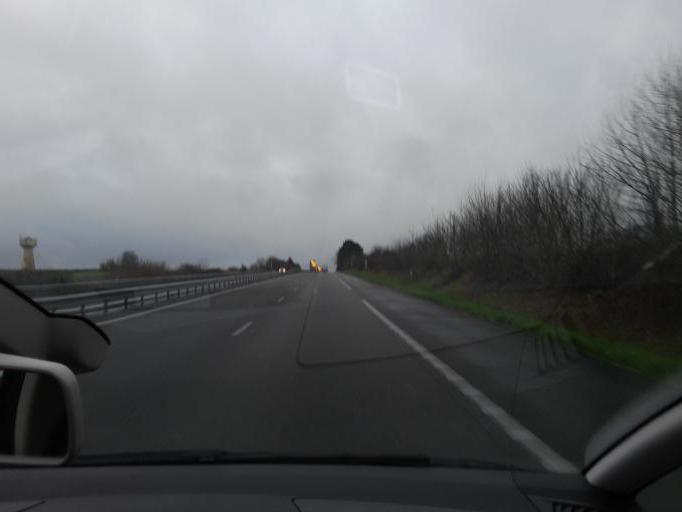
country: FR
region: Nord-Pas-de-Calais
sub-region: Departement du Pas-de-Calais
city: Hermies
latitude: 50.1142
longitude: 3.0778
